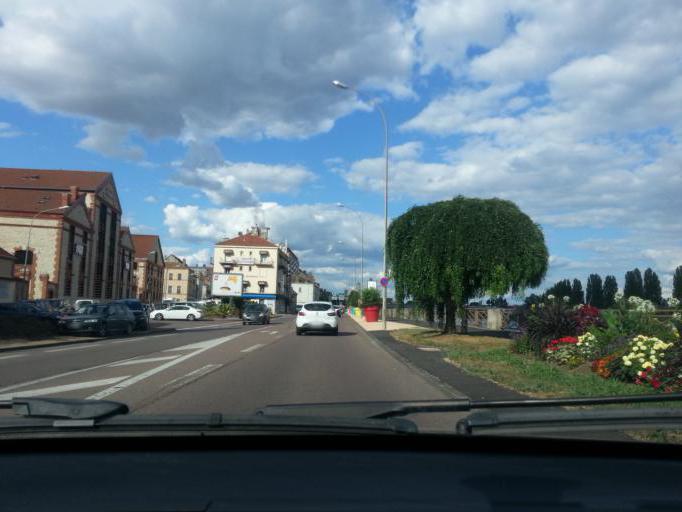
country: FR
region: Bourgogne
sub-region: Departement de Saone-et-Loire
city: Chalon-sur-Saone
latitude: 46.7759
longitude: 4.8469
